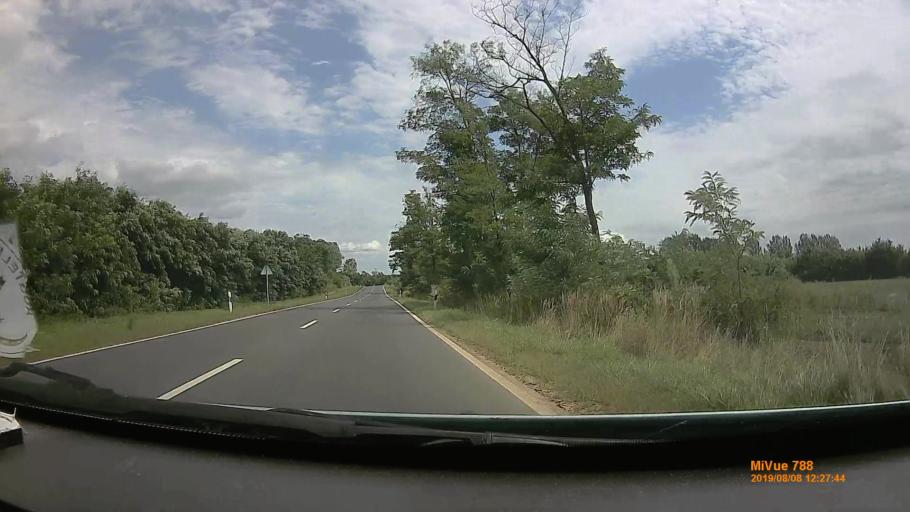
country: HU
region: Szabolcs-Szatmar-Bereg
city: Nyirbator
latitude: 47.8249
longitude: 22.1028
